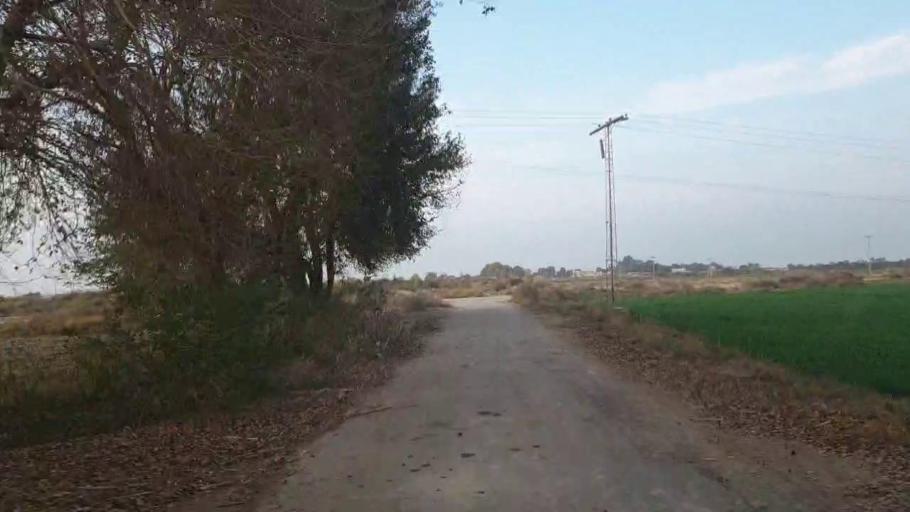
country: PK
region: Sindh
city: Shahpur Chakar
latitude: 26.1179
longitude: 68.5443
